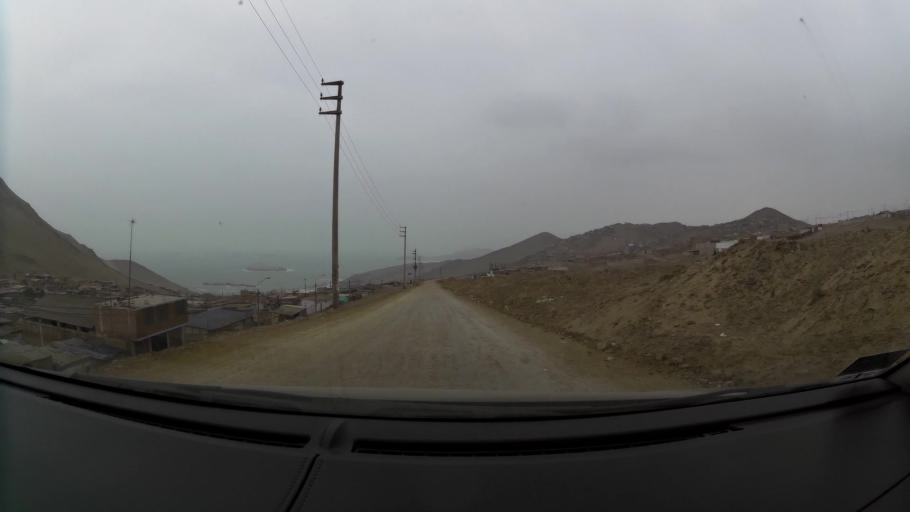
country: PE
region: Lima
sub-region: Lima
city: Santa Rosa
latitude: -11.8209
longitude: -77.1653
